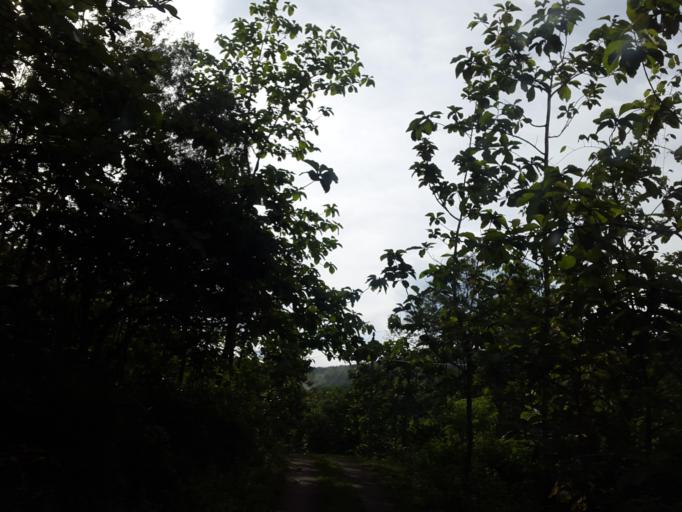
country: ID
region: Central Java
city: Trucuk
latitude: -7.8161
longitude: 110.6804
